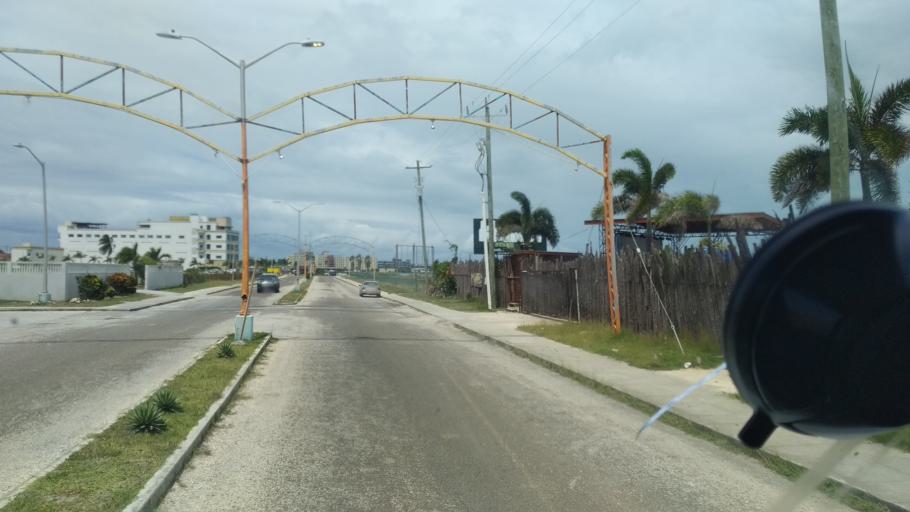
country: BZ
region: Belize
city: Belize City
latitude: 17.4986
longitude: -88.1820
